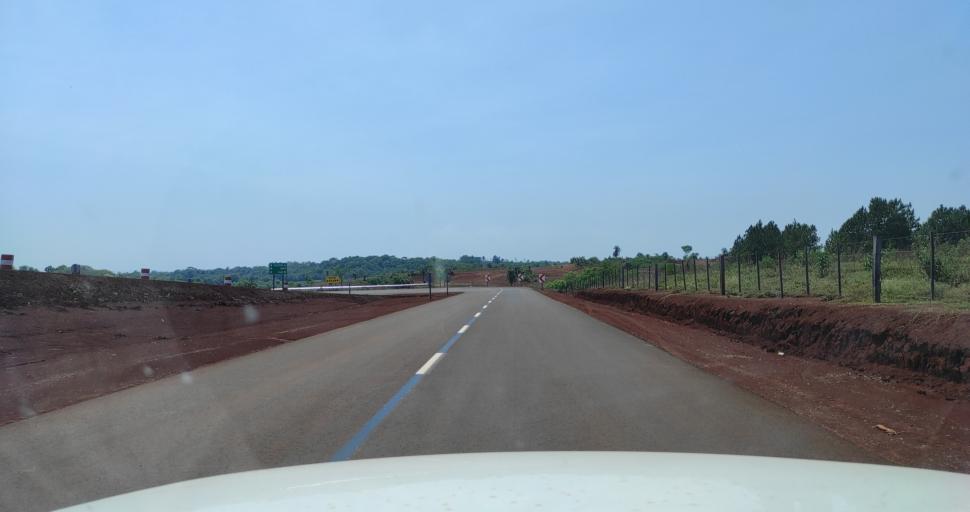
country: AR
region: Misiones
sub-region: Departamento de Candelaria
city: Loreto
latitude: -27.3386
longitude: -55.5440
